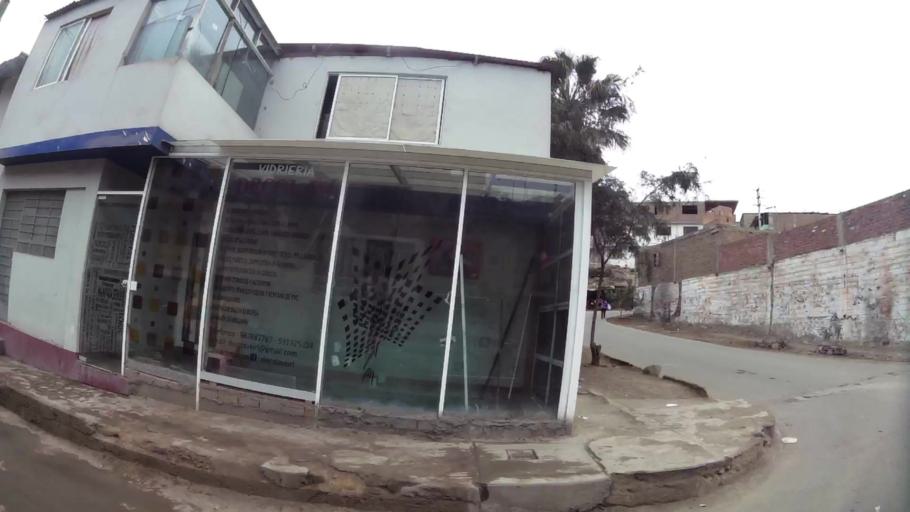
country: PE
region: Lima
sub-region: Lima
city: Surco
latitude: -12.1374
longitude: -76.9723
